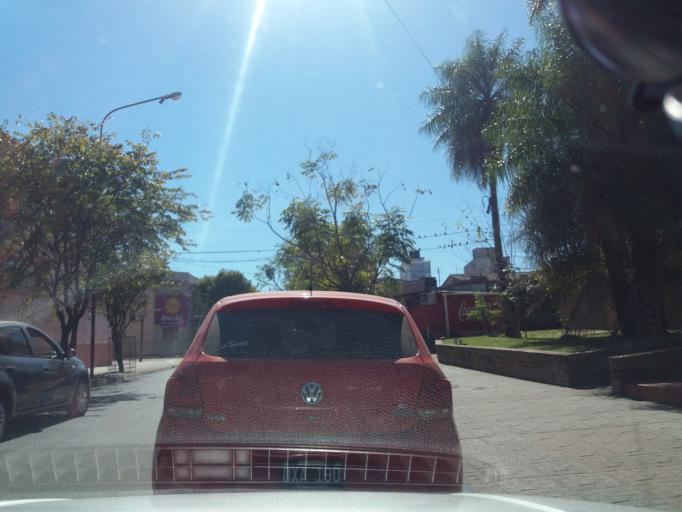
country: AR
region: Corrientes
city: Corrientes
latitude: -27.4748
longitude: -58.8363
